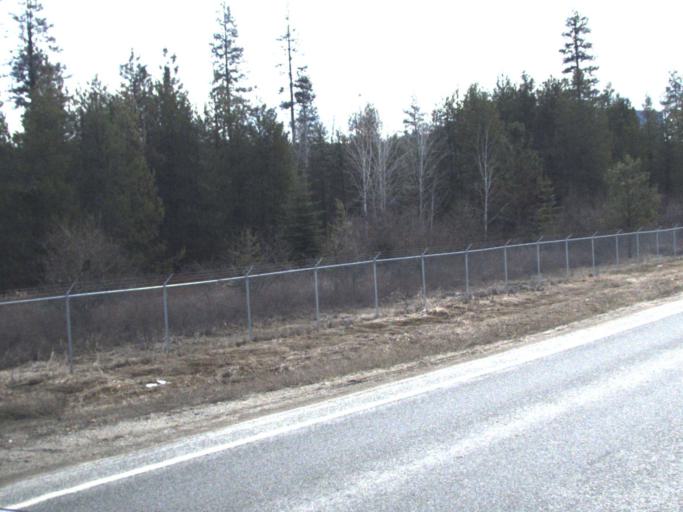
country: US
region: Washington
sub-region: Pend Oreille County
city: Newport
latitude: 48.2914
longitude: -117.2747
